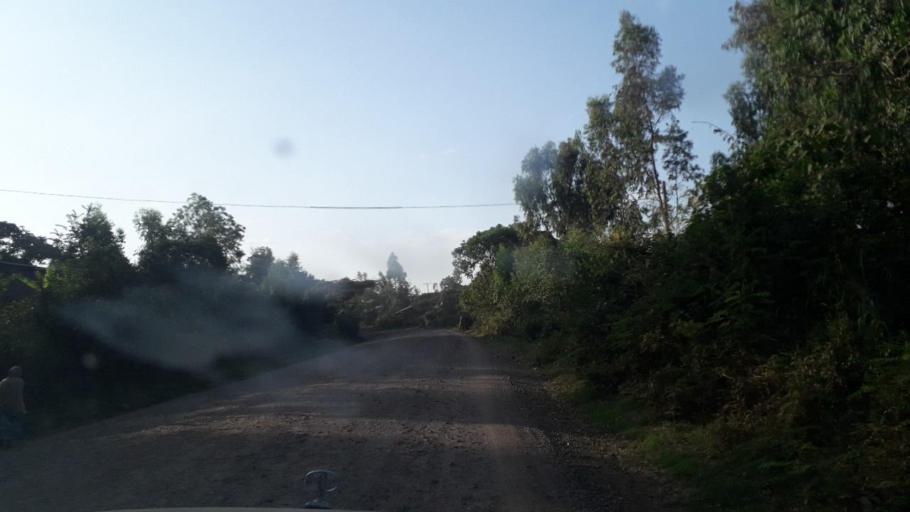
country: ET
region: Oromiya
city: Jima
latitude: 7.5910
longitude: 36.8553
